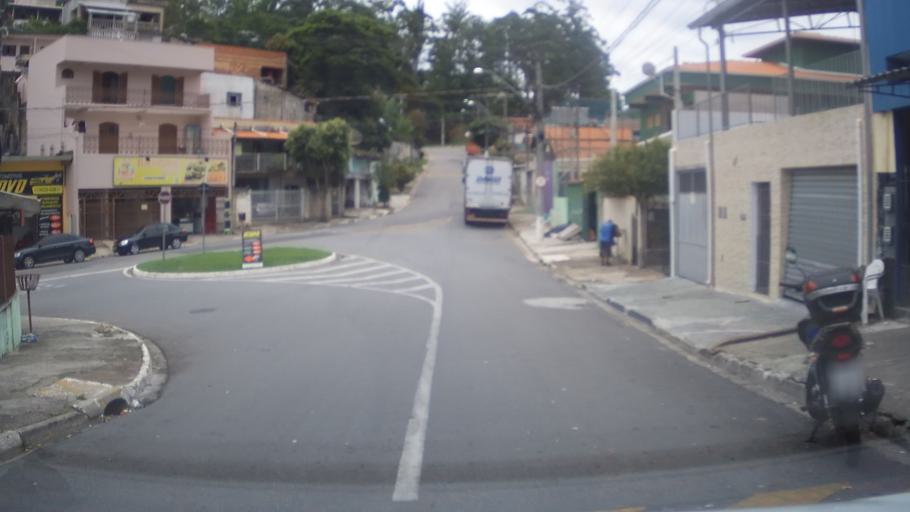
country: BR
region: Sao Paulo
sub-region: Louveira
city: Louveira
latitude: -23.0804
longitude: -46.9814
